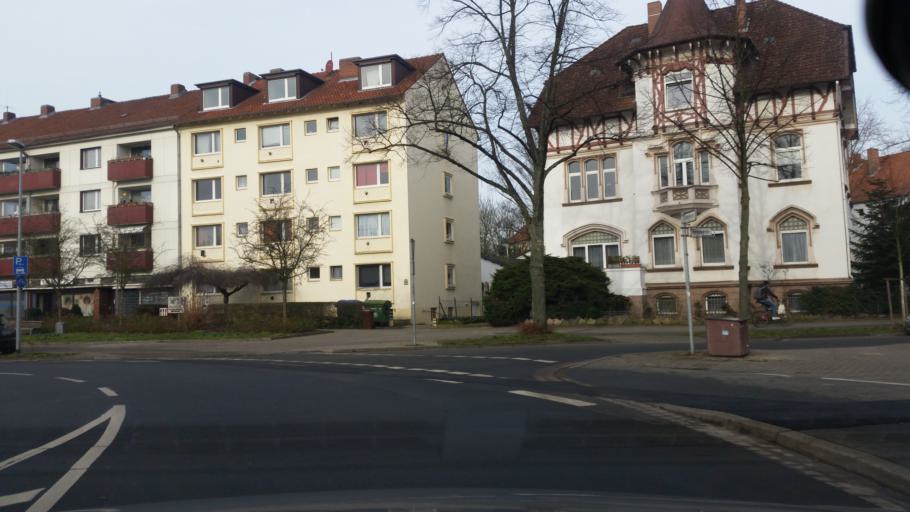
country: DE
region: Lower Saxony
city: Hannover
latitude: 52.3978
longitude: 9.7211
